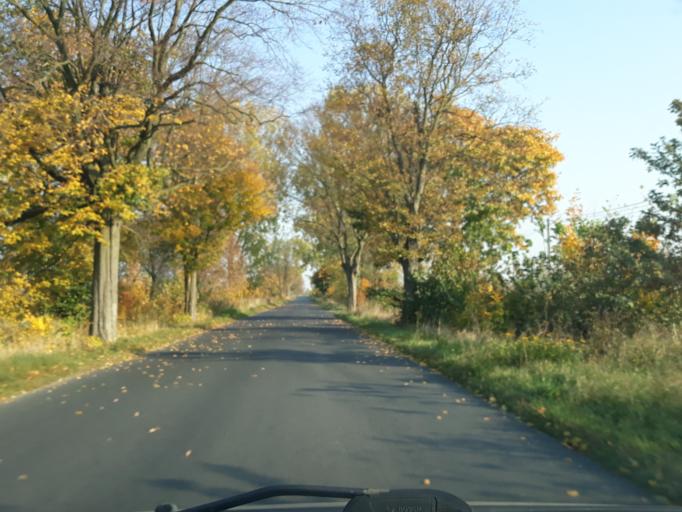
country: PL
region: Kujawsko-Pomorskie
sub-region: Powiat sepolenski
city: Sepolno Krajenskie
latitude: 53.4707
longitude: 17.4843
